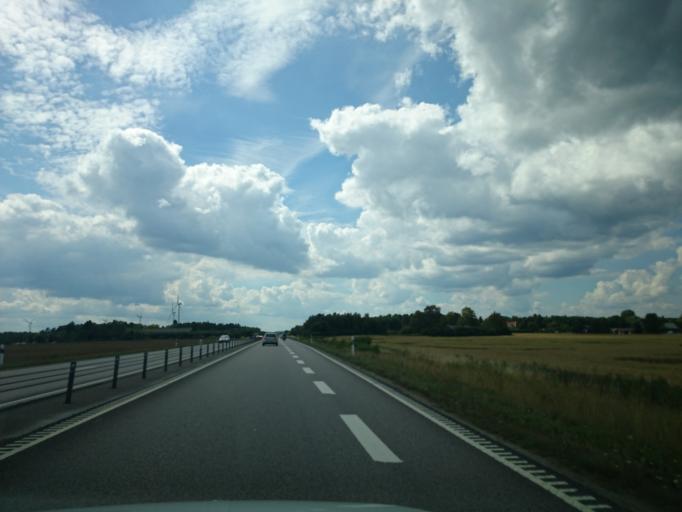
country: SE
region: Kalmar
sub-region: Kalmar Kommun
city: Ljungbyholm
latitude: 56.6243
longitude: 16.1766
